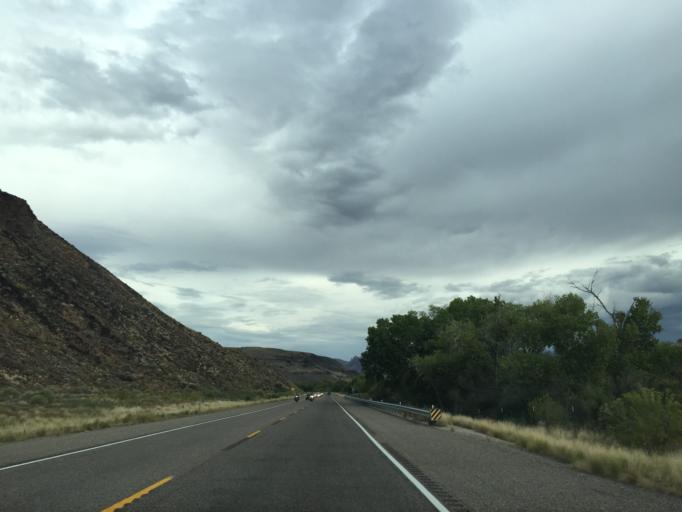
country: US
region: Utah
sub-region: Washington County
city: LaVerkin
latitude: 37.1822
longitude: -113.1320
